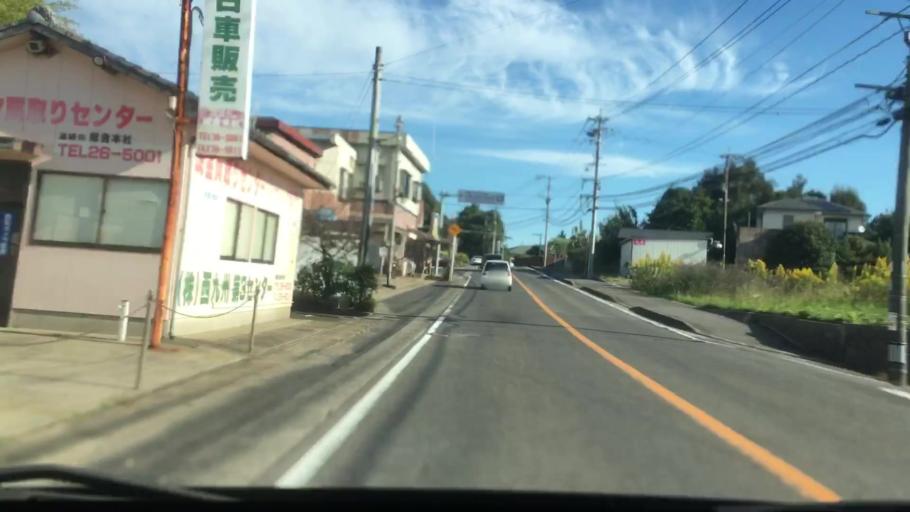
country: JP
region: Nagasaki
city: Sasebo
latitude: 33.0615
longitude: 129.7636
